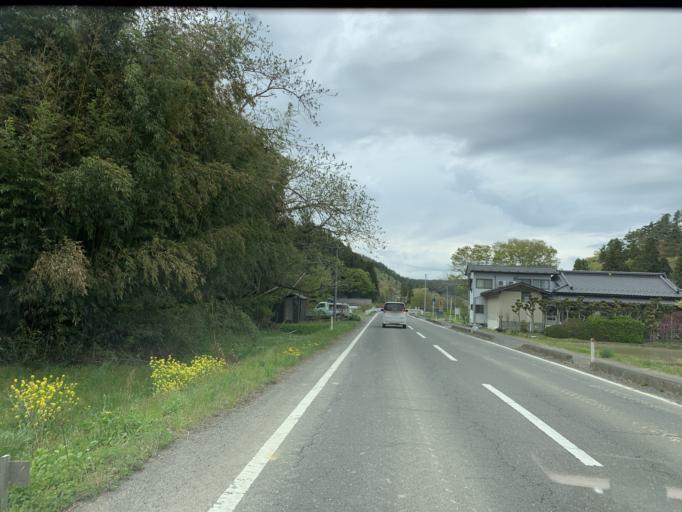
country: JP
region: Iwate
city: Ichinoseki
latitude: 38.7817
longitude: 141.3274
